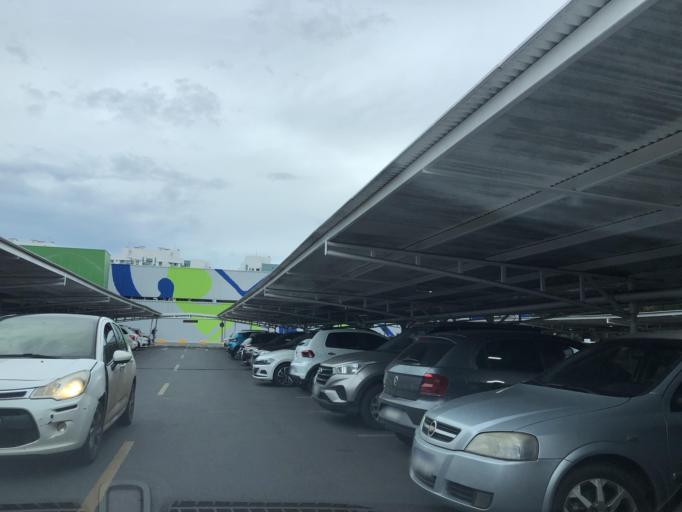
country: BR
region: Federal District
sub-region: Brasilia
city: Brasilia
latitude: -15.8301
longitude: -47.9540
